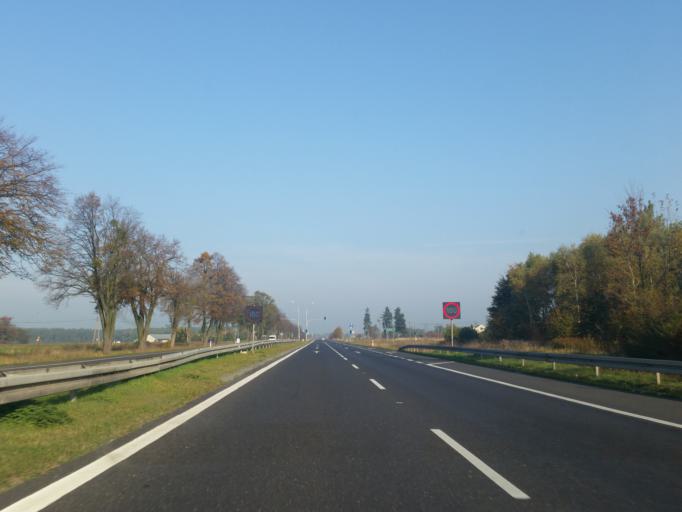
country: PL
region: Masovian Voivodeship
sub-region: Powiat plonski
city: Zaluski
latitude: 52.4857
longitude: 20.5498
